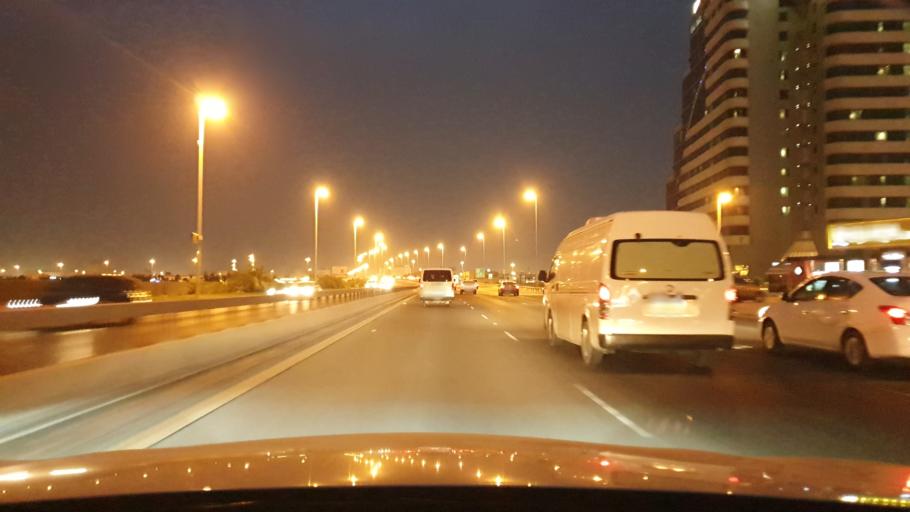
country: BH
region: Muharraq
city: Al Muharraq
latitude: 26.2455
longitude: 50.6006
